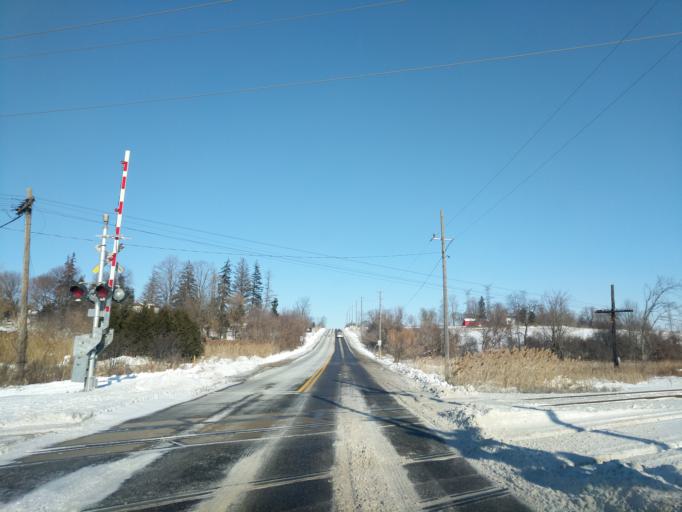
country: CA
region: Ontario
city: Pickering
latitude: 43.8480
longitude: -79.1284
